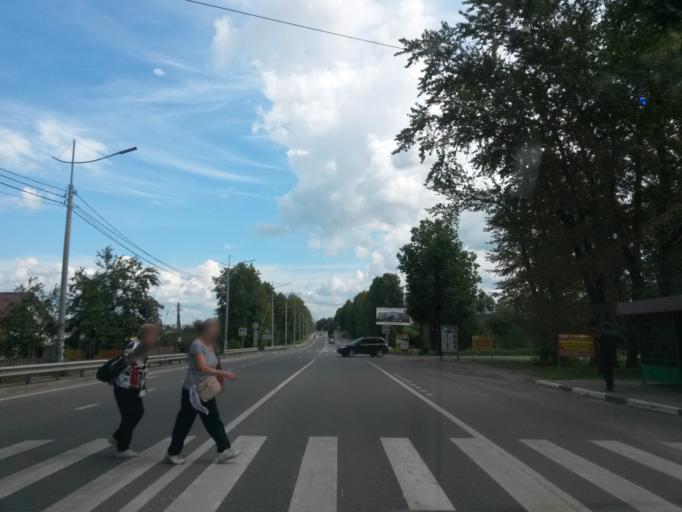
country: RU
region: Jaroslavl
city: Pereslavl'-Zalesskiy
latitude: 56.7114
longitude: 38.8113
